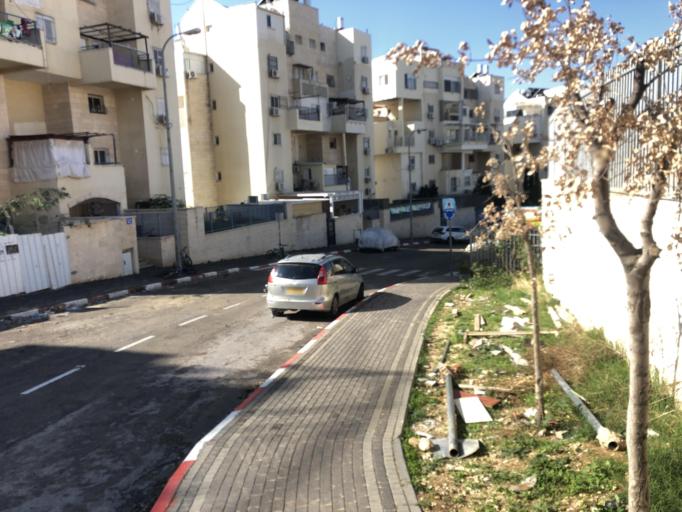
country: IL
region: Jerusalem
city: Modiin Ilit
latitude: 31.9232
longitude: 35.0506
